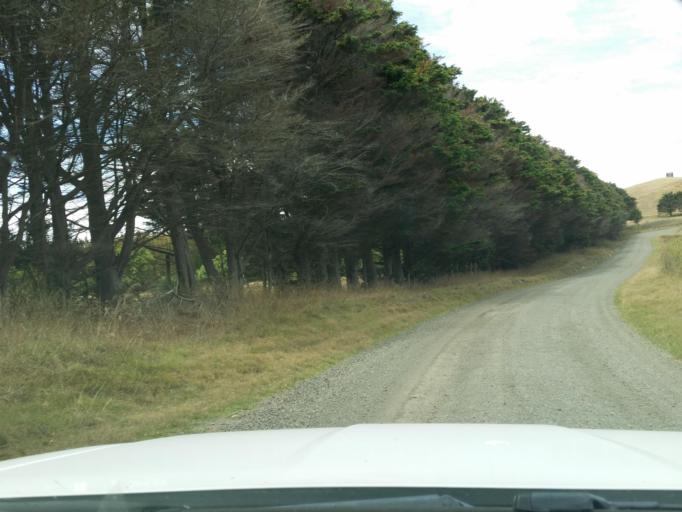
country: NZ
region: Auckland
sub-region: Auckland
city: Wellsford
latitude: -36.3422
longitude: 174.1669
